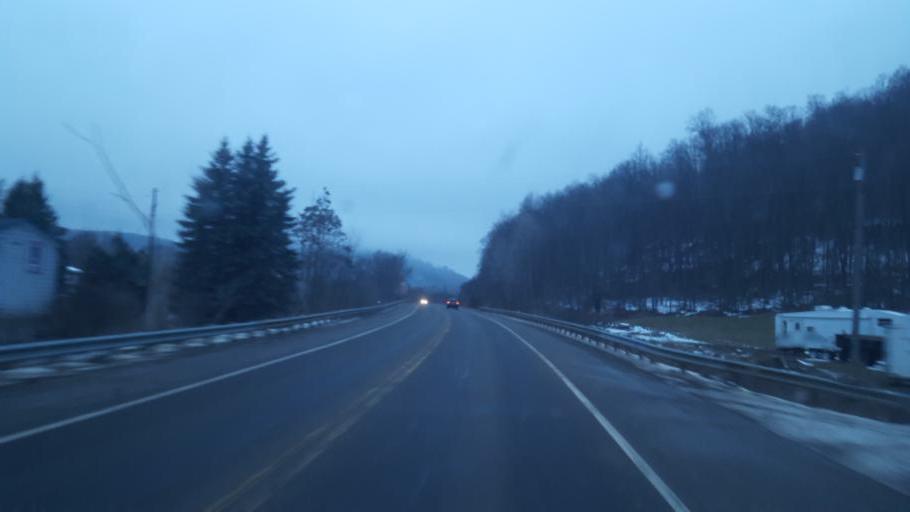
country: US
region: Pennsylvania
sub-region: Potter County
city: Coudersport
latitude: 41.7776
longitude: -78.1357
